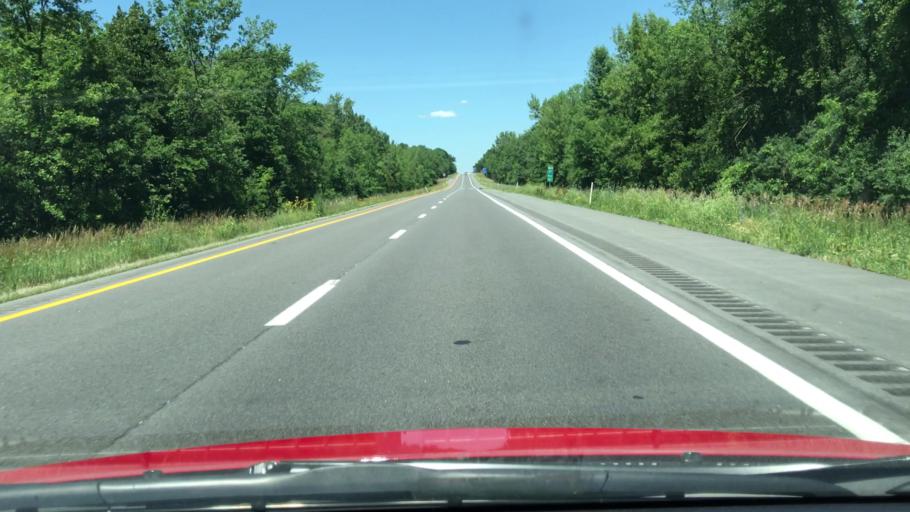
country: US
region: New York
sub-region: Clinton County
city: Cumberland Head
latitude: 44.7949
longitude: -73.4411
